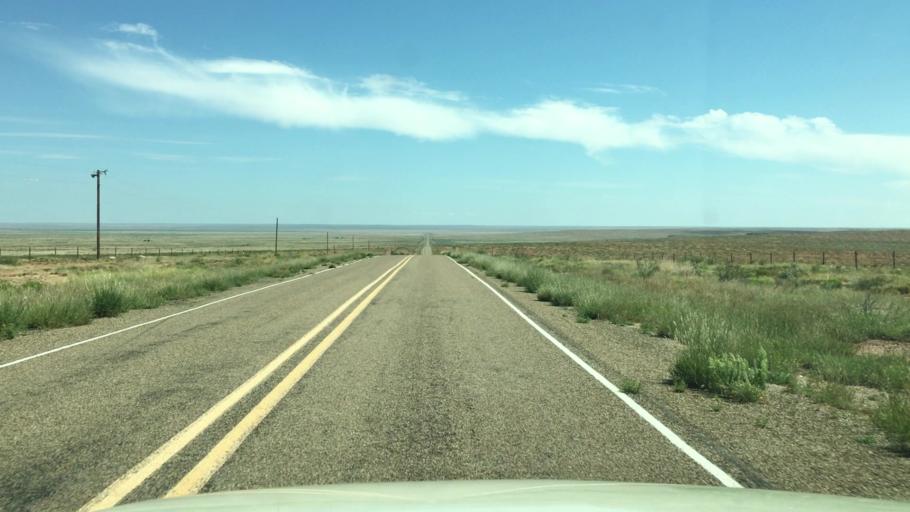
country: US
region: New Mexico
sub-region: Chaves County
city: Roswell
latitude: 33.9672
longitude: -104.5809
